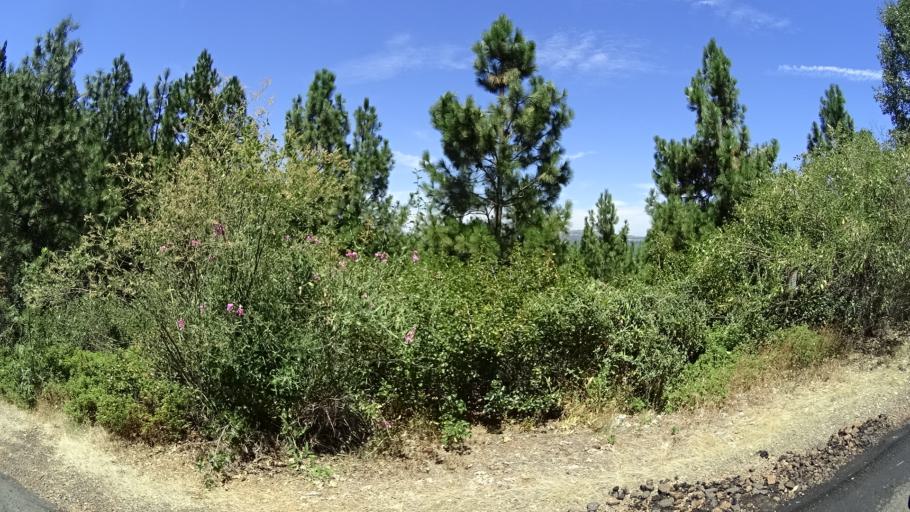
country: US
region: California
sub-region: Calaveras County
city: Forest Meadows
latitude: 38.1976
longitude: -120.4228
